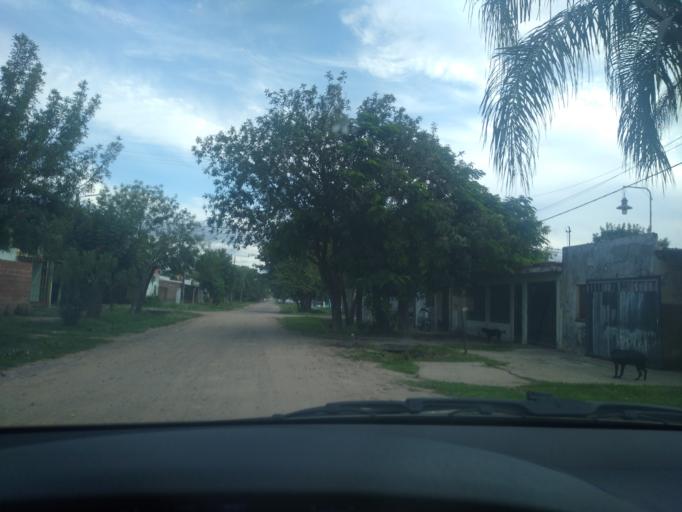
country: AR
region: Chaco
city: Resistencia
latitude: -27.4802
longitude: -58.9726
